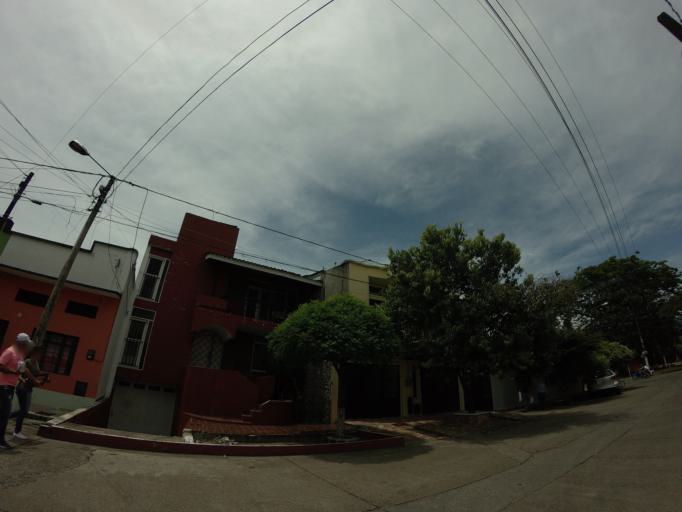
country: CO
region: Caldas
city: La Dorada
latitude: 5.4480
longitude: -74.6661
